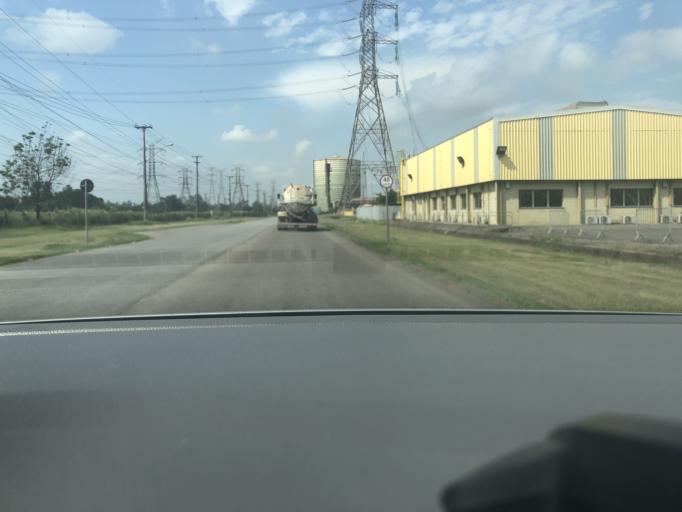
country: BR
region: Rio de Janeiro
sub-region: Itaguai
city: Itaguai
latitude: -22.9104
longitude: -43.7459
